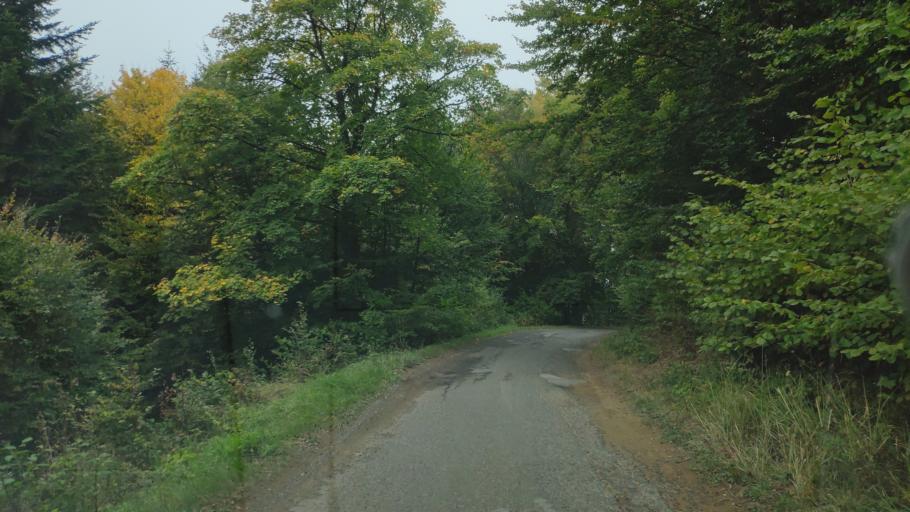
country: SK
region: Presovsky
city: Giraltovce
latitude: 48.9157
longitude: 21.4580
